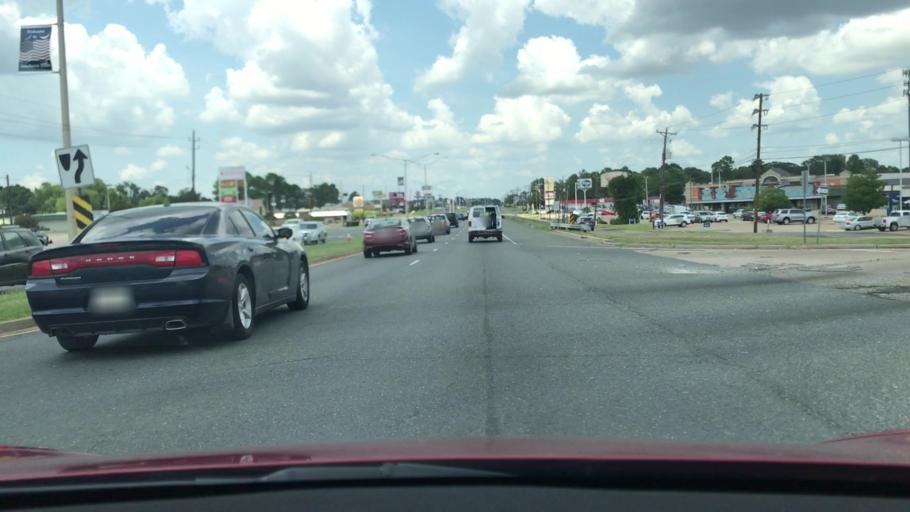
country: US
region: Louisiana
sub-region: De Soto Parish
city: Stonewall
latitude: 32.4021
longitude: -93.8041
